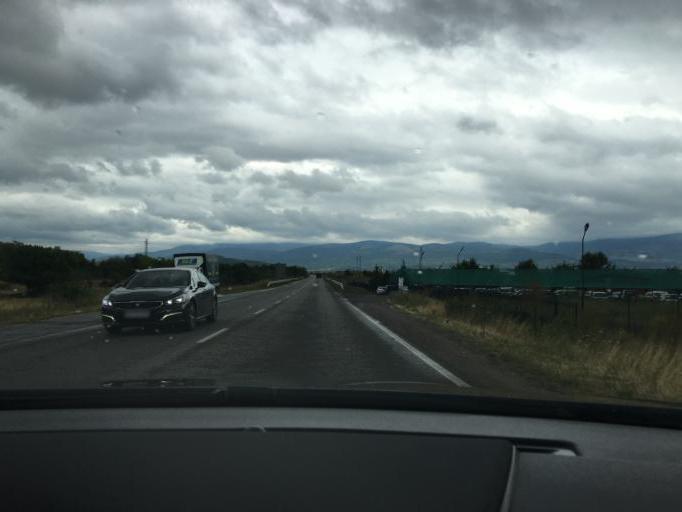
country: BG
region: Kyustendil
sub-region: Obshtina Kyustendil
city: Kyustendil
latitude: 42.2836
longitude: 22.7198
